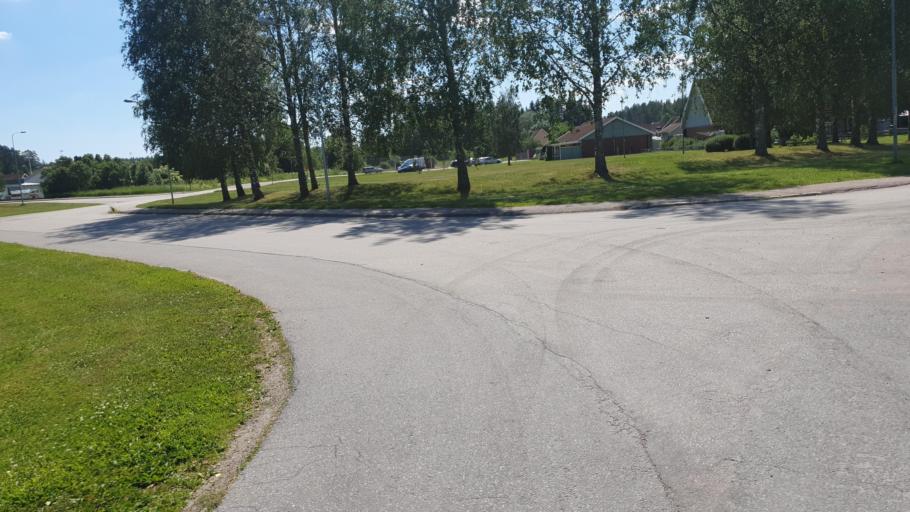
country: SE
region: Uppsala
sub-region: Osthammars Kommun
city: Gimo
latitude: 60.1726
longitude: 18.1747
